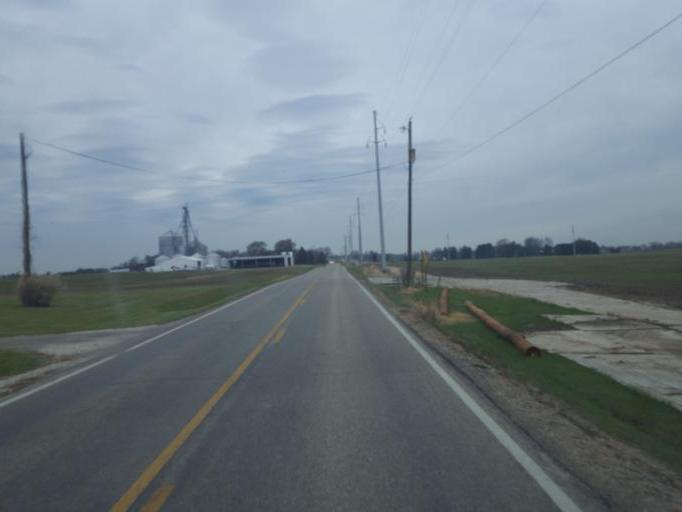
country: US
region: Ohio
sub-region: Delaware County
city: Delaware
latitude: 40.3607
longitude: -83.0997
